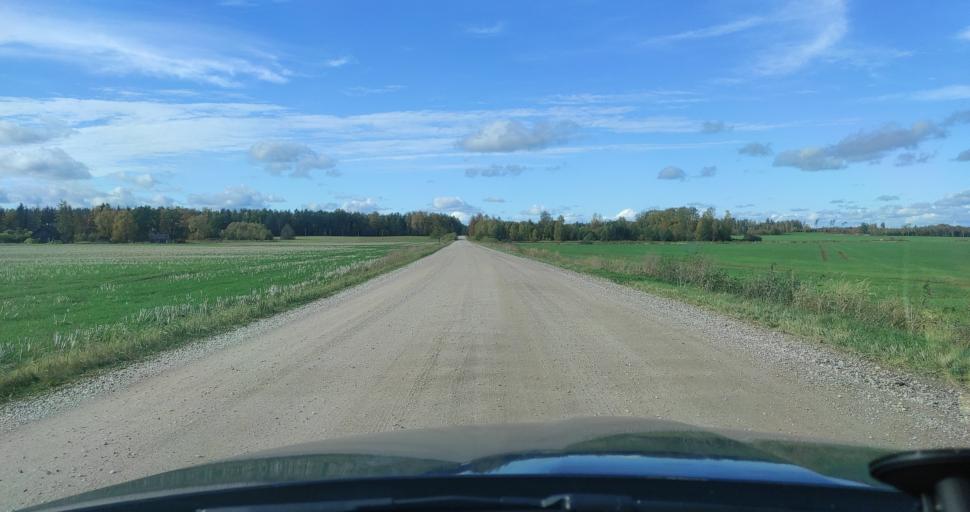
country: LV
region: Jaunpils
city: Jaunpils
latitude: 56.8283
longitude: 23.0199
